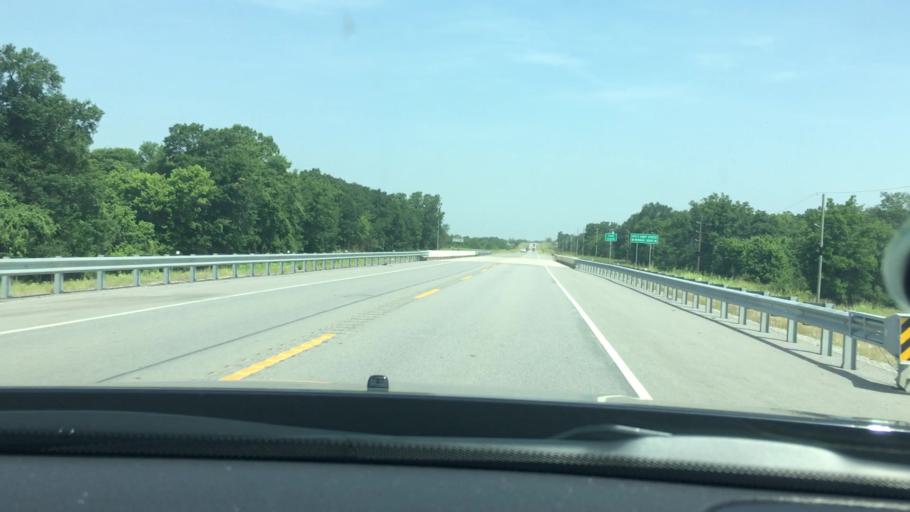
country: US
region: Oklahoma
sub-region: Coal County
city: Coalgate
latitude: 34.4446
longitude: -96.2061
